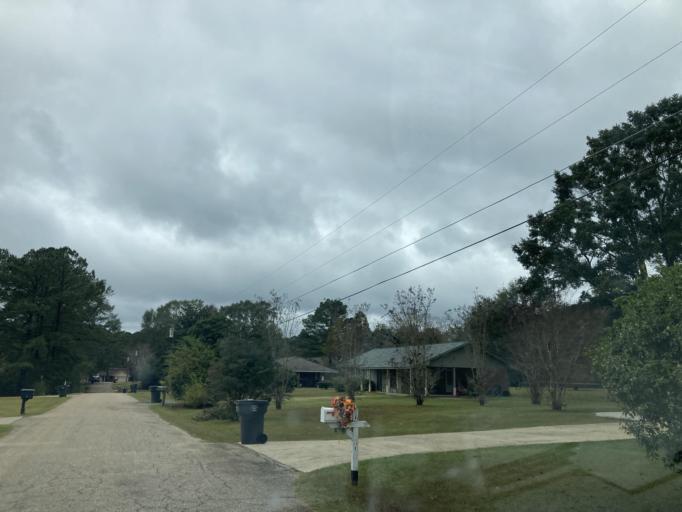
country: US
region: Mississippi
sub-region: Lamar County
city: West Hattiesburg
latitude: 31.2908
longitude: -89.4749
